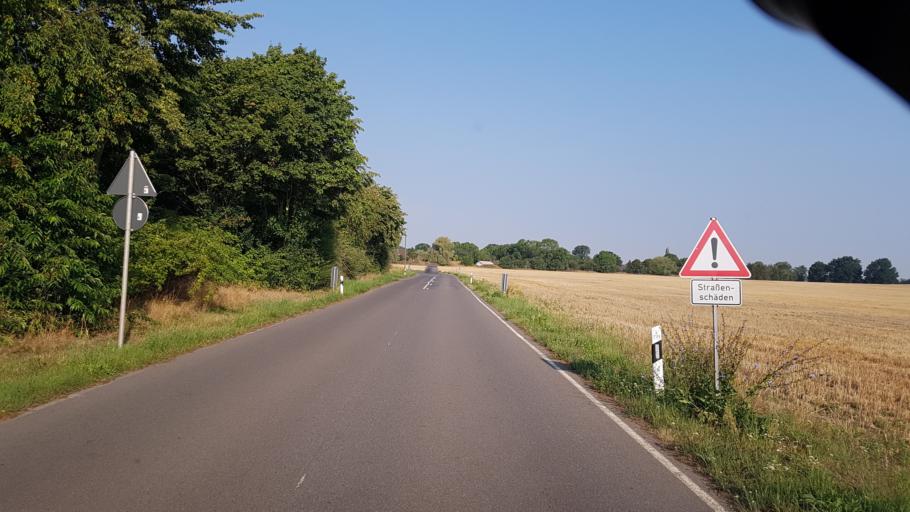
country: DE
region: Brandenburg
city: Drebkau
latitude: 51.6678
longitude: 14.2390
